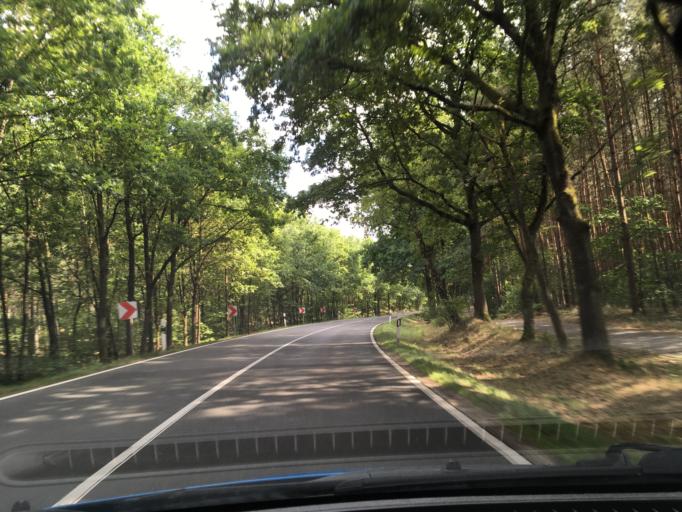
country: DE
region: Mecklenburg-Vorpommern
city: Lubtheen
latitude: 53.2909
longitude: 11.0921
